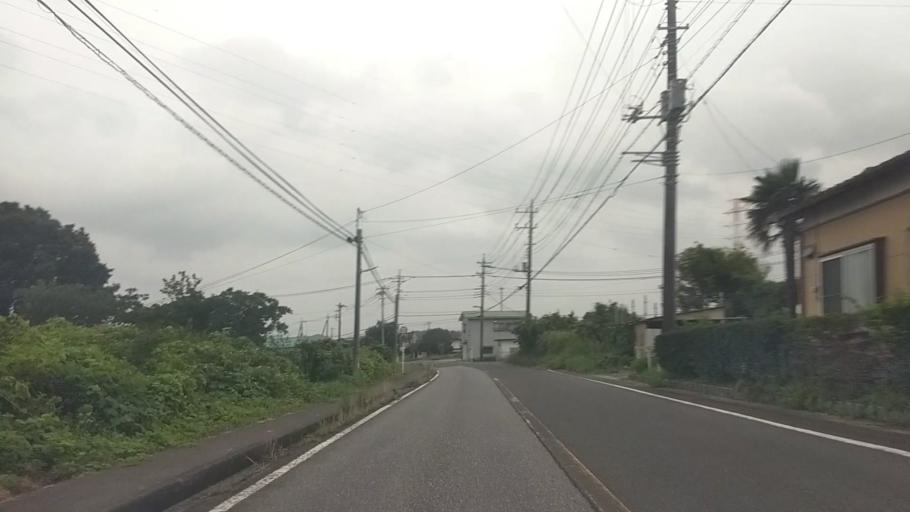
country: JP
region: Chiba
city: Kisarazu
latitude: 35.3862
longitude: 140.0409
